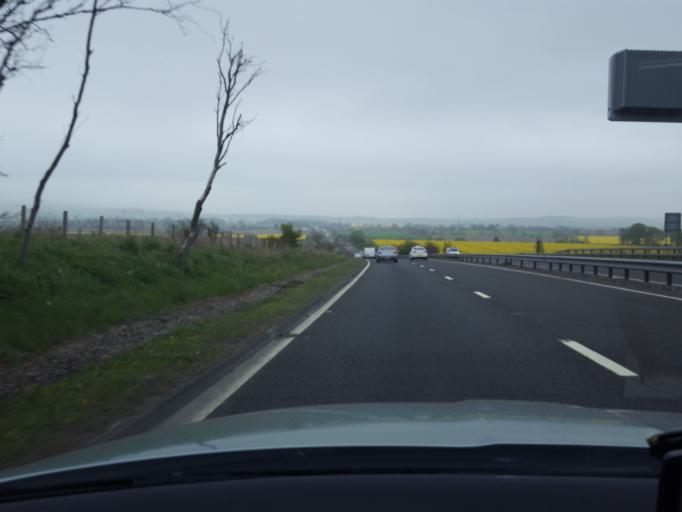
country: GB
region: Scotland
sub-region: Dundee City
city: Dundee
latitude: 56.5063
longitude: -2.9465
